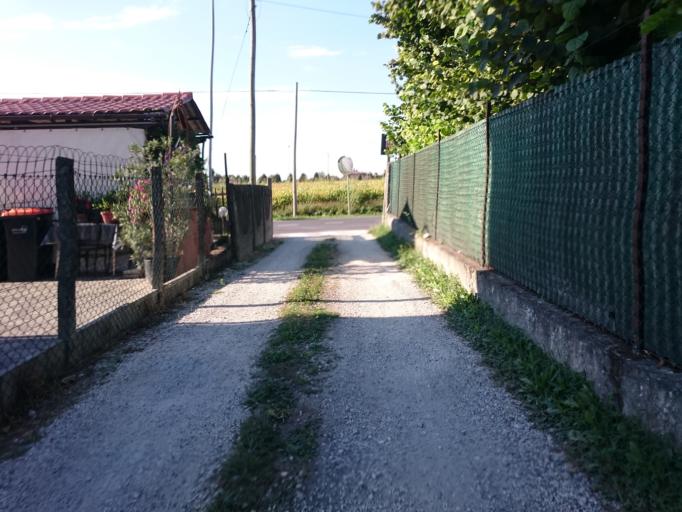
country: IT
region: Veneto
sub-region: Provincia di Padova
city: Albignasego
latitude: 45.3393
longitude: 11.8941
